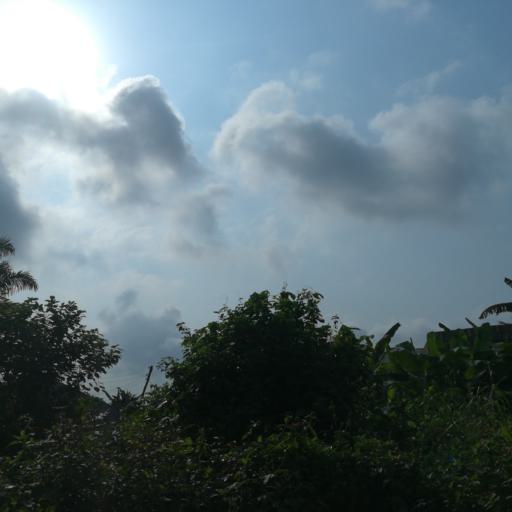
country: NG
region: Rivers
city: Okrika
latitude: 4.7805
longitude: 7.1376
